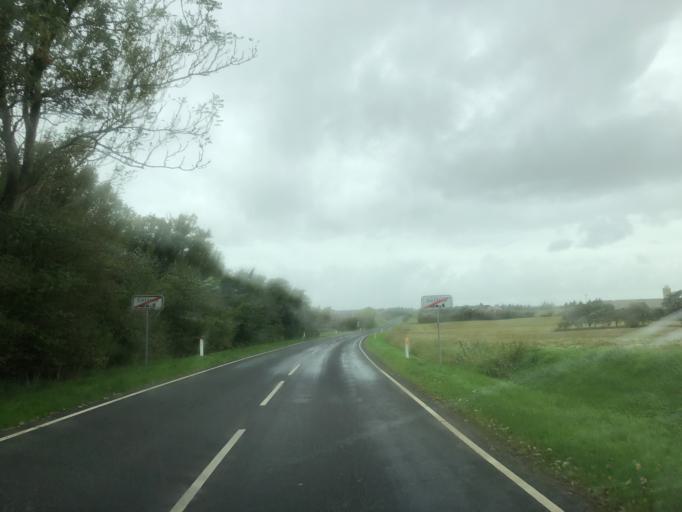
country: DK
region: North Denmark
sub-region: Thisted Kommune
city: Hurup
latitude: 56.7222
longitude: 8.3521
